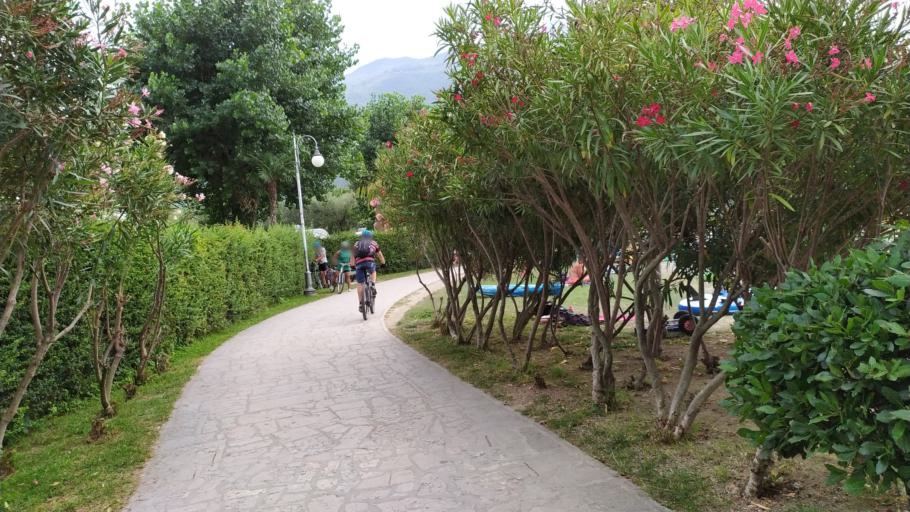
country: IT
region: Trentino-Alto Adige
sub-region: Provincia di Trento
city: Torbole sul Garda
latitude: 45.8756
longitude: 10.8669
